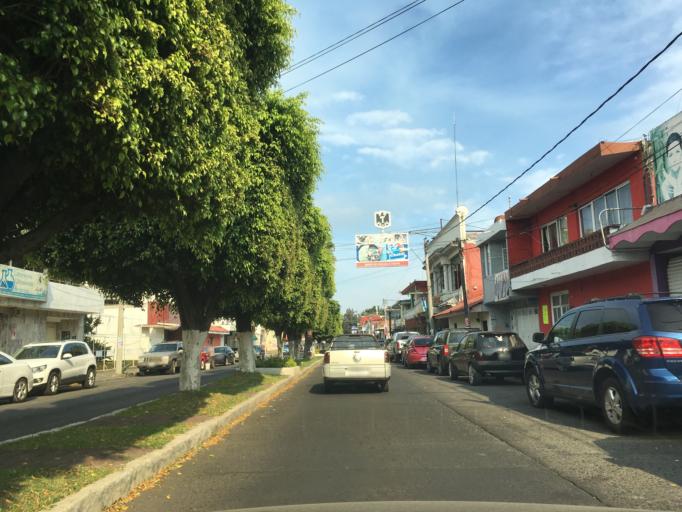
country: MX
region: Michoacan
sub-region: Uruapan
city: Uruapan
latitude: 19.4159
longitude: -102.0552
